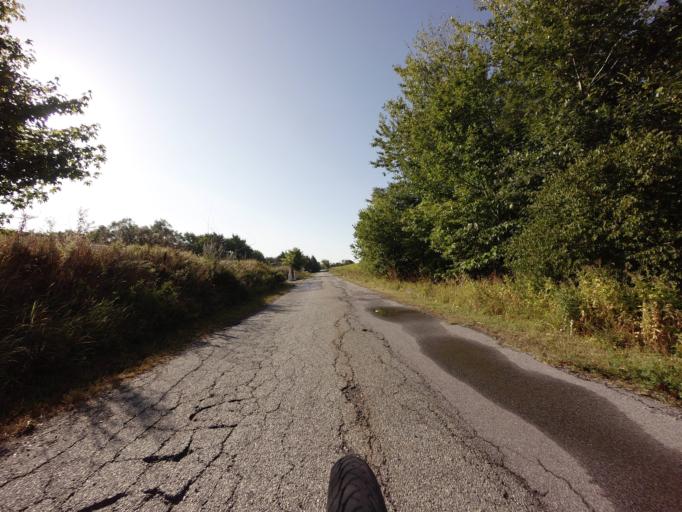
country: DK
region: North Denmark
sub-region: Hjorring Kommune
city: Vra
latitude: 57.3856
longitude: 9.9598
